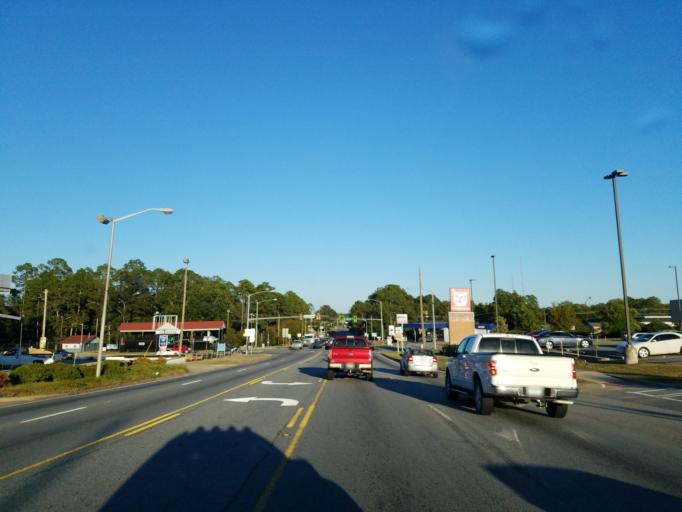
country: US
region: Georgia
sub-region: Worth County
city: Sylvester
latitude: 31.5306
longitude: -83.8365
